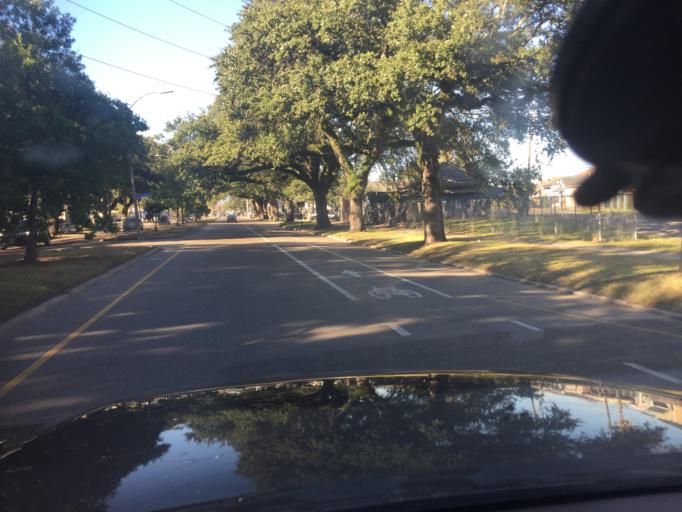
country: US
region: Louisiana
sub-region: Orleans Parish
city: New Orleans
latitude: 29.9802
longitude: -90.0699
